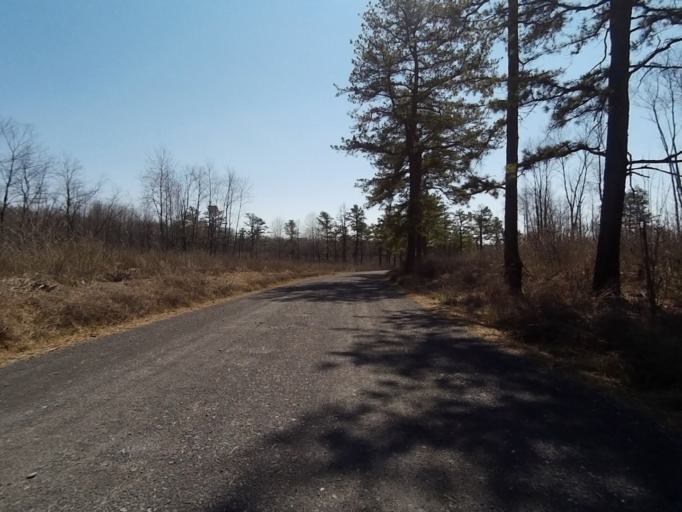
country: US
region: Pennsylvania
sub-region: Centre County
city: Park Forest Village
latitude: 40.7834
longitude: -77.9497
